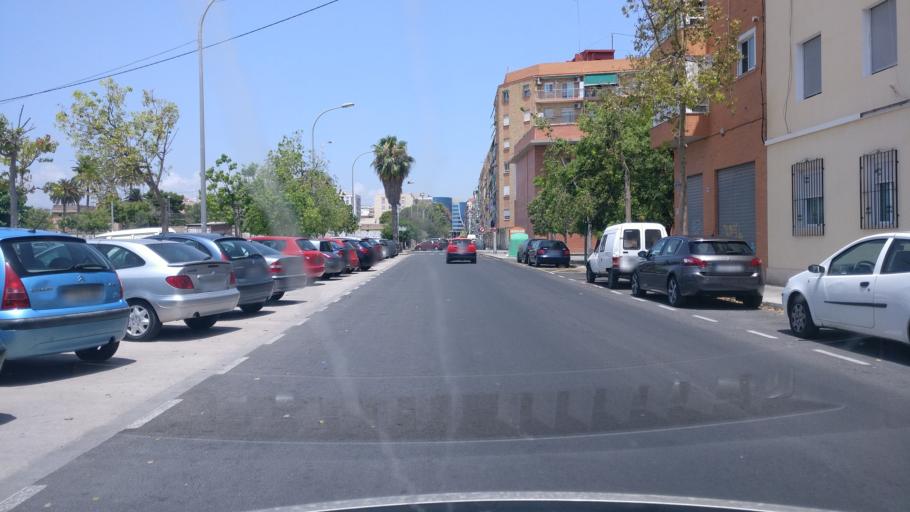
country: ES
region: Valencia
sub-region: Provincia de Valencia
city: Alboraya
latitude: 39.4793
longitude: -0.3298
